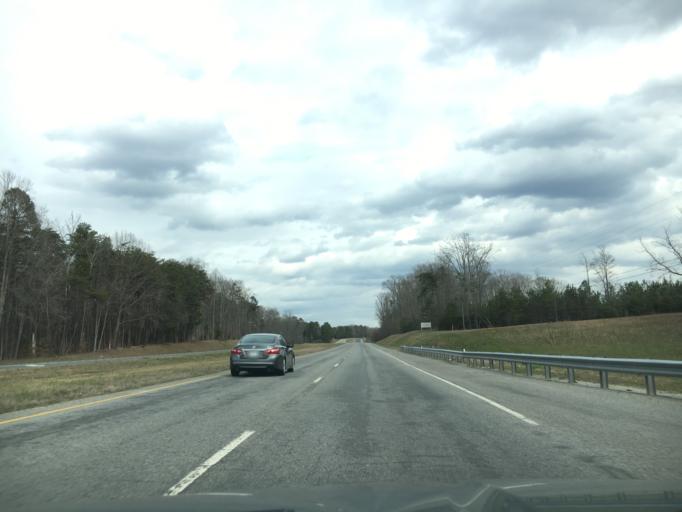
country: US
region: Virginia
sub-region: Mecklenburg County
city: Boydton
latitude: 36.6576
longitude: -78.4420
